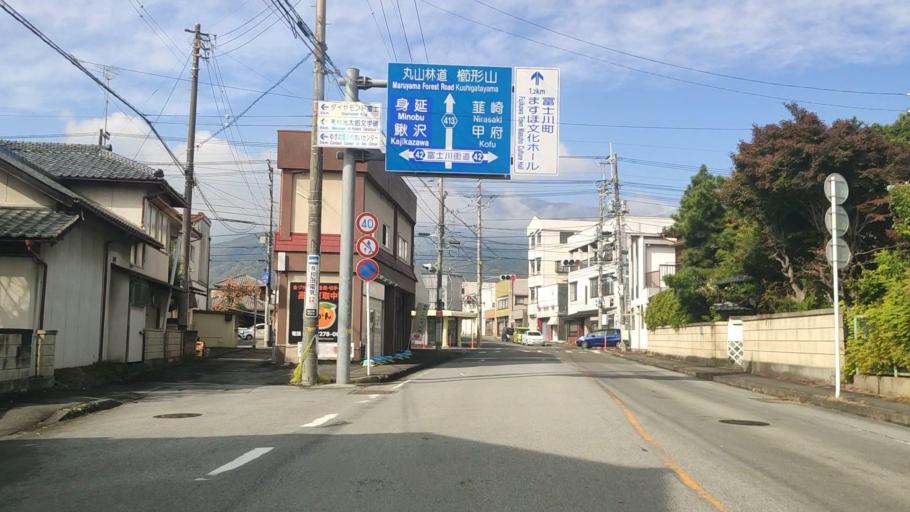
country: JP
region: Yamanashi
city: Ryuo
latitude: 35.5600
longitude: 138.4666
